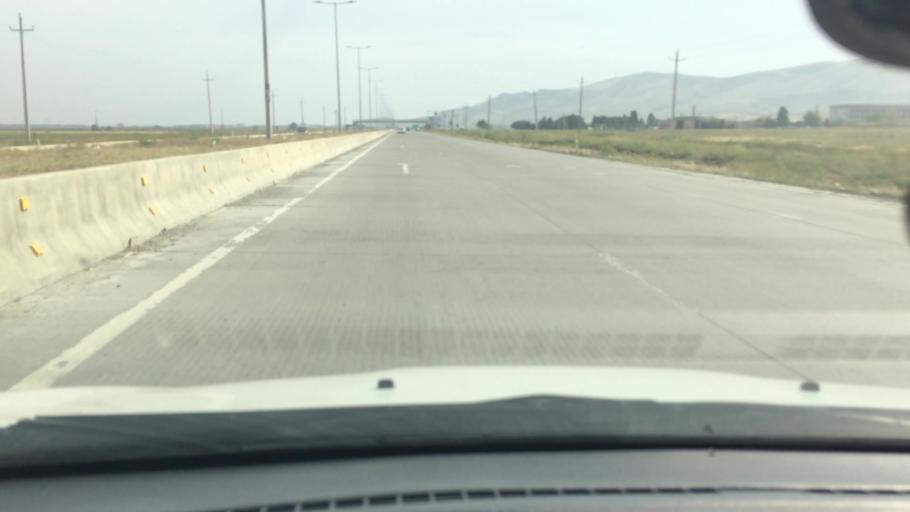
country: GE
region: Kvemo Kartli
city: Rust'avi
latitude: 41.5981
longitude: 44.9422
